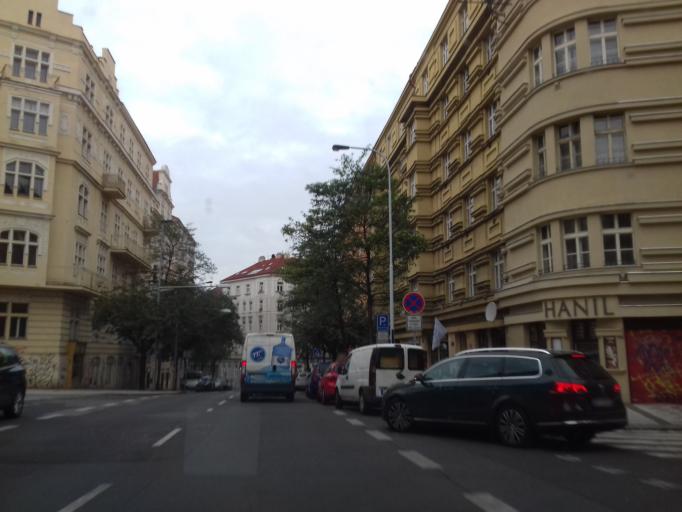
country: CZ
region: Praha
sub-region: Praha 8
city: Karlin
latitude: 50.0806
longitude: 14.4465
